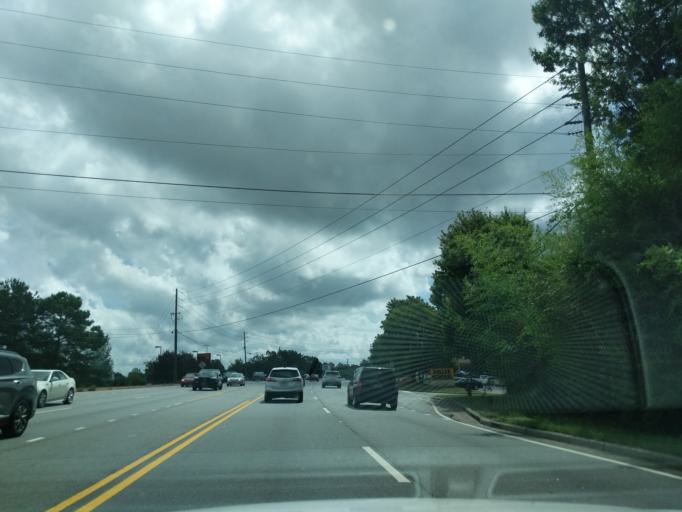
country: US
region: Georgia
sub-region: Columbia County
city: Evans
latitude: 33.5419
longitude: -82.1354
